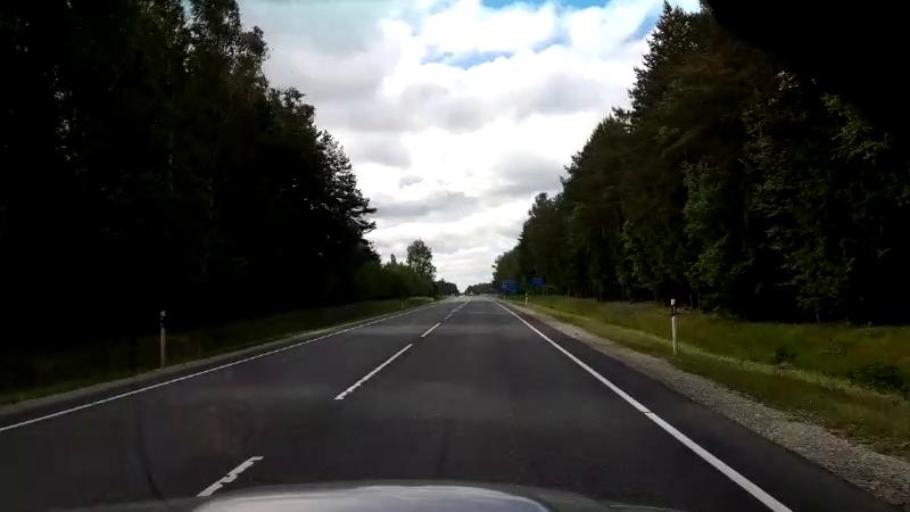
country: EE
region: Raplamaa
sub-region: Maerjamaa vald
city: Marjamaa
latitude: 58.8140
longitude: 24.4124
